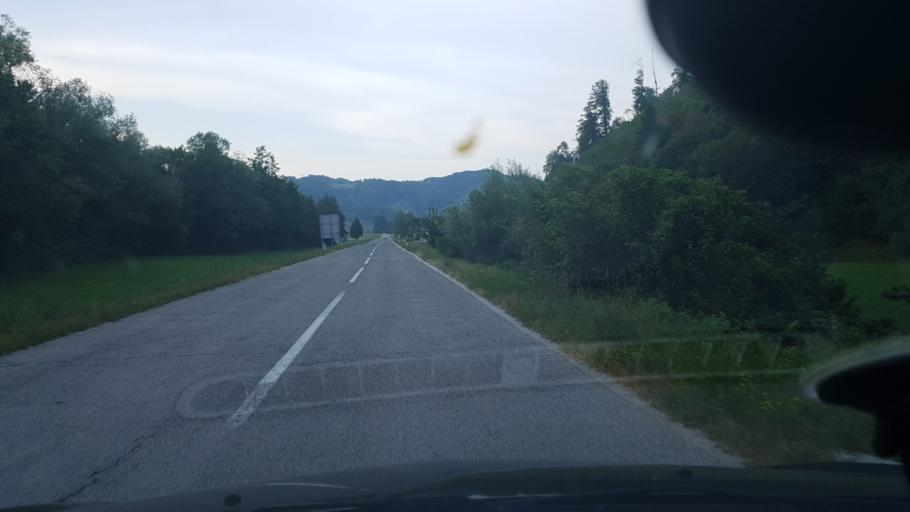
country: SI
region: Kozje
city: Kozje
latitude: 46.0402
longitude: 15.5923
